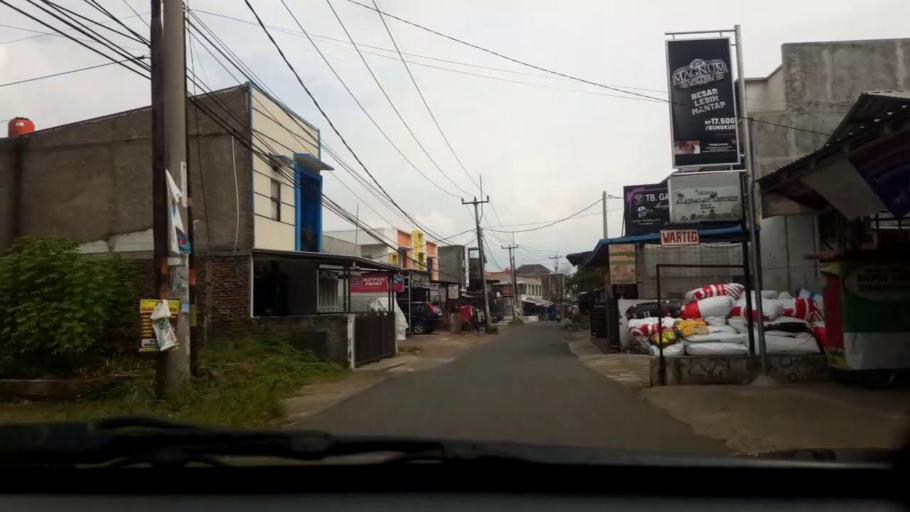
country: ID
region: West Java
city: Cileunyi
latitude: -6.9430
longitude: 107.7259
